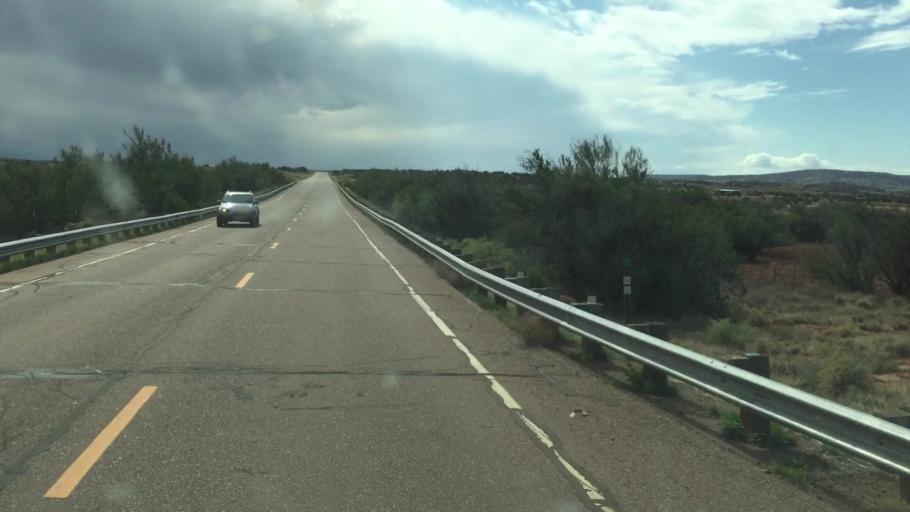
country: US
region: Arizona
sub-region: Apache County
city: Saint Johns
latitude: 34.5148
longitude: -109.6992
